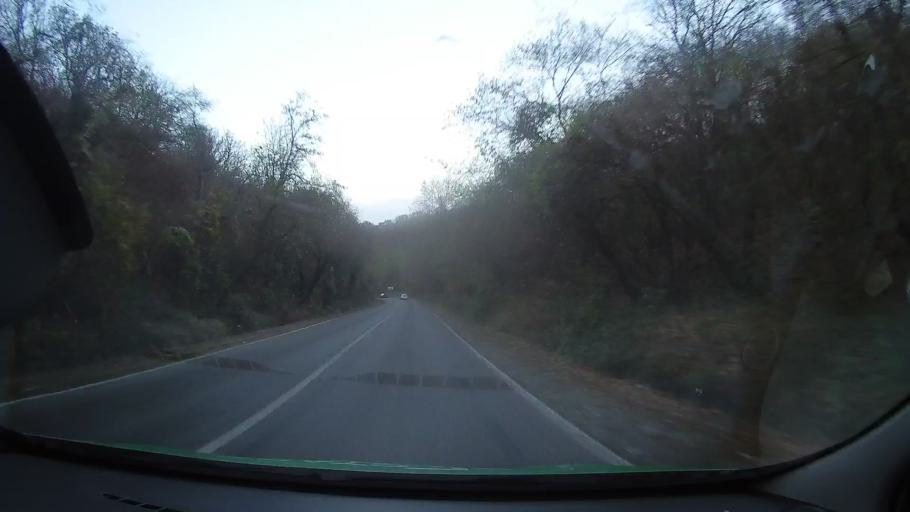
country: RO
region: Constanta
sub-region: Comuna Baneasa
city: Baneasa
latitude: 44.0924
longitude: 27.6534
